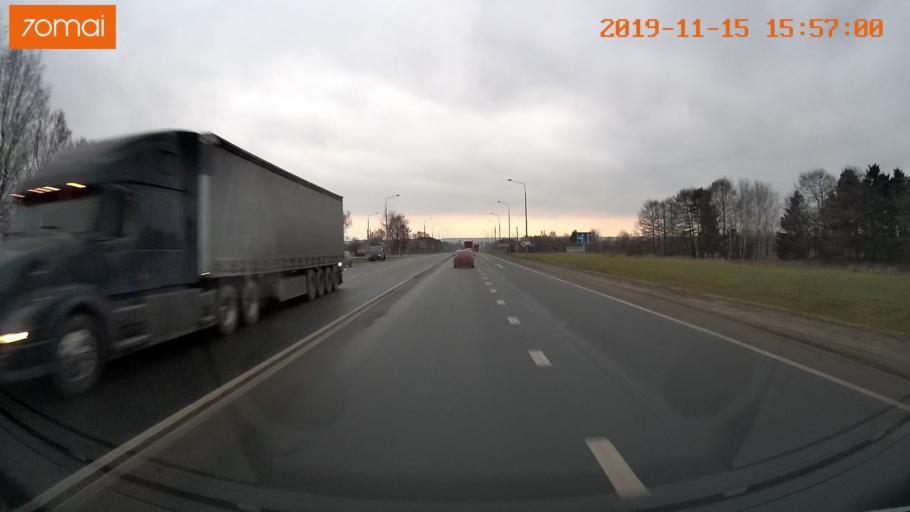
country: RU
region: Jaroslavl
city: Yaroslavl
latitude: 57.8355
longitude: 39.9679
